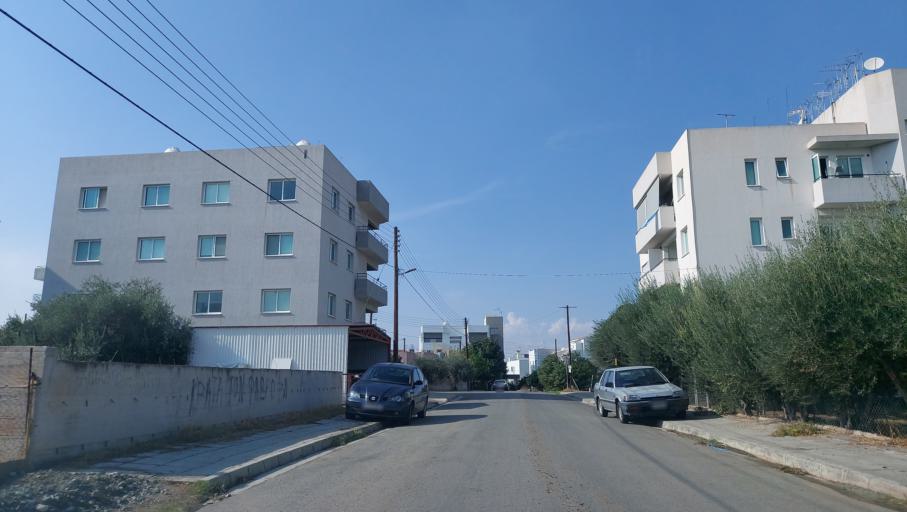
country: CY
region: Lefkosia
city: Tseri
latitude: 35.1056
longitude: 33.3067
